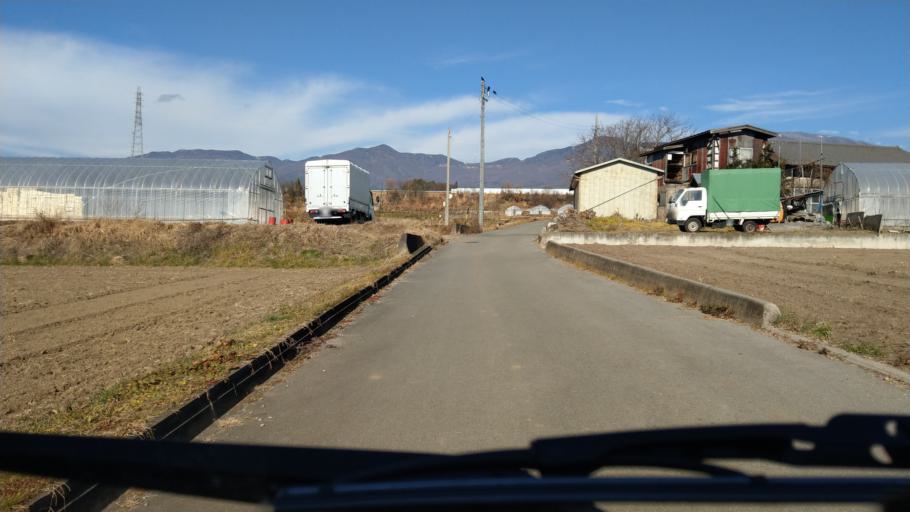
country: JP
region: Nagano
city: Komoro
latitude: 36.3255
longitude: 138.4545
